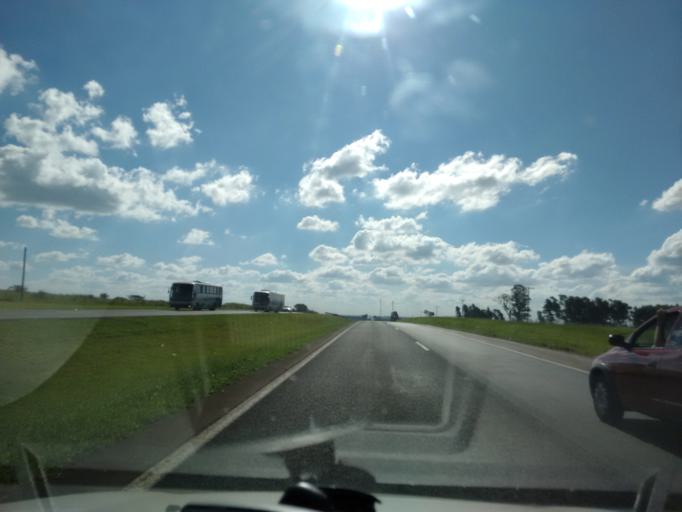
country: BR
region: Sao Paulo
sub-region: Ibate
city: Ibate
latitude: -21.9213
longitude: -48.0332
